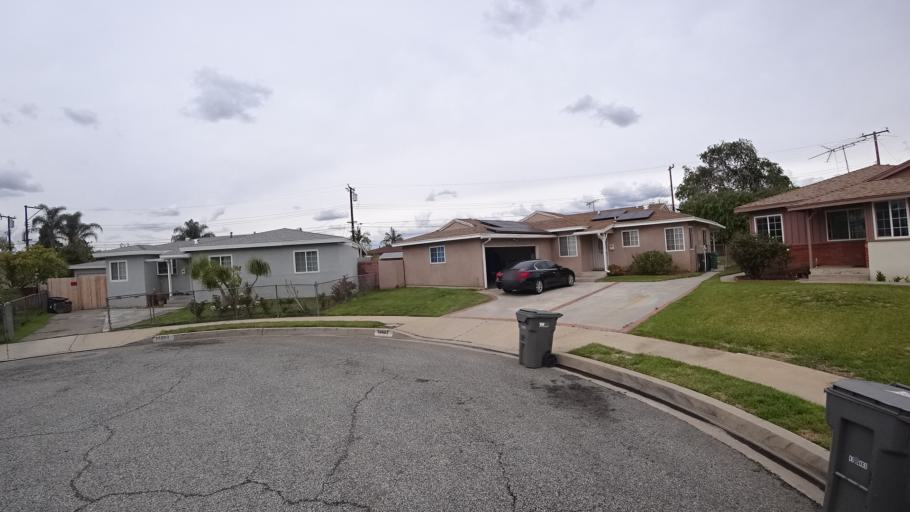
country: US
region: California
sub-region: Los Angeles County
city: West Puente Valley
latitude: 34.0670
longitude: -117.9627
